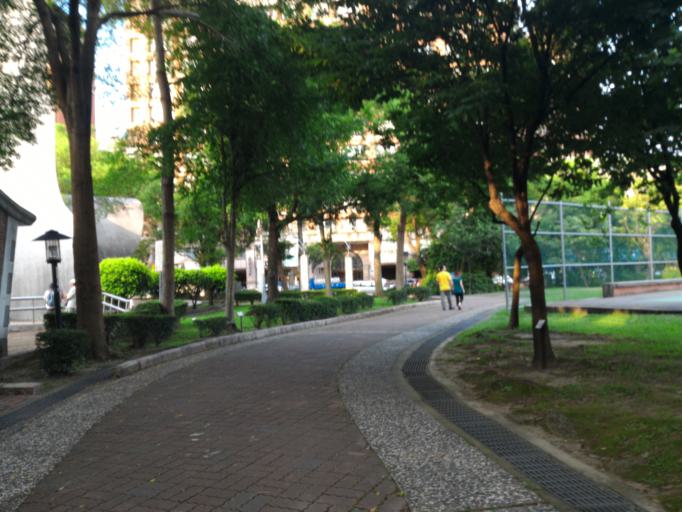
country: TW
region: Taipei
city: Taipei
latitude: 25.0028
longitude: 121.5142
